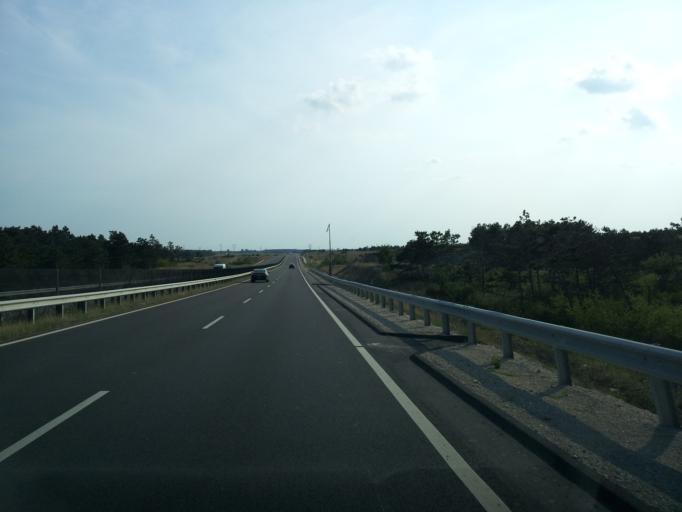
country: HU
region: Veszprem
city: Hajmasker
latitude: 47.1290
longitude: 18.0059
